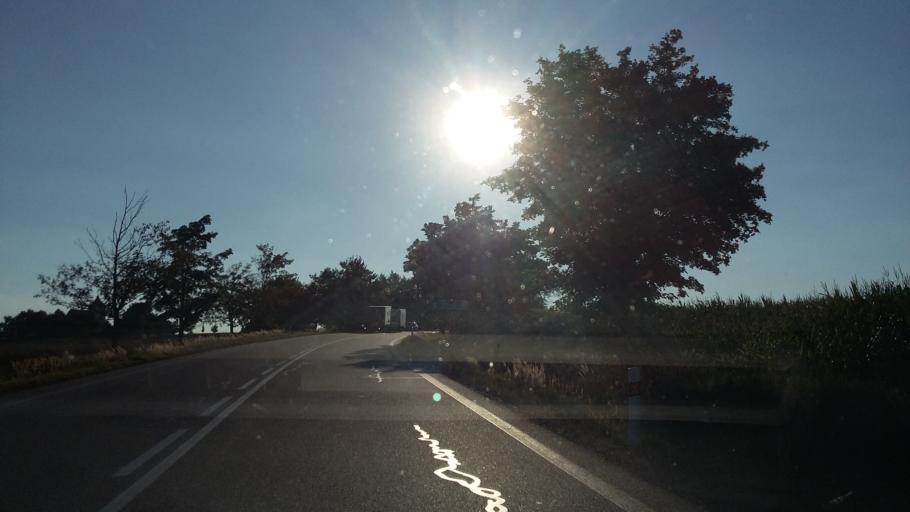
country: CZ
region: Vysocina
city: Luka nad Jihlavou
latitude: 49.3957
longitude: 15.7403
